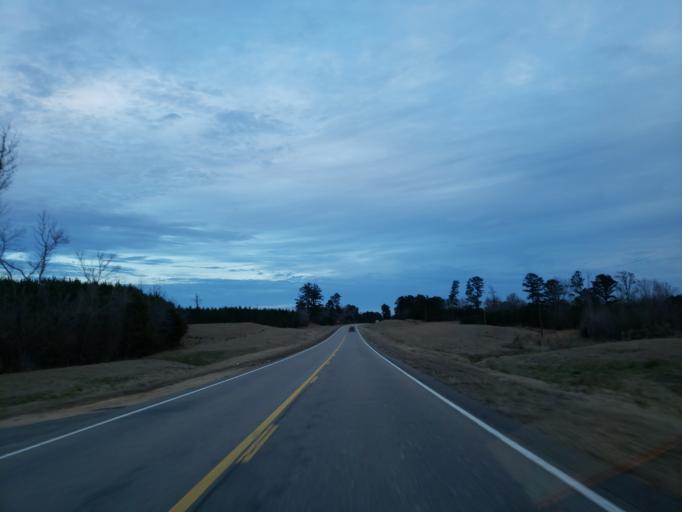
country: US
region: Mississippi
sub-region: Kemper County
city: De Kalb
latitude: 32.8309
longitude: -88.3690
